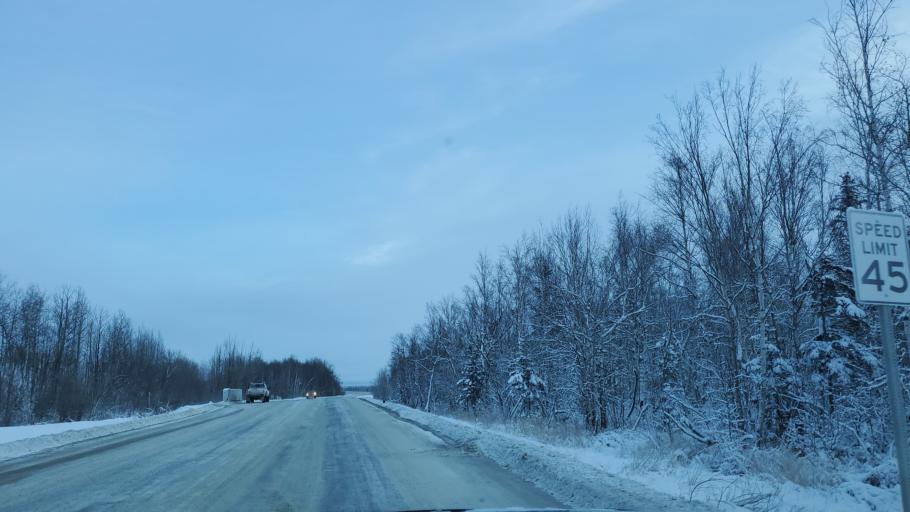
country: US
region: Alaska
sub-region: Matanuska-Susitna Borough
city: Gateway
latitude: 61.5505
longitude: -149.2923
